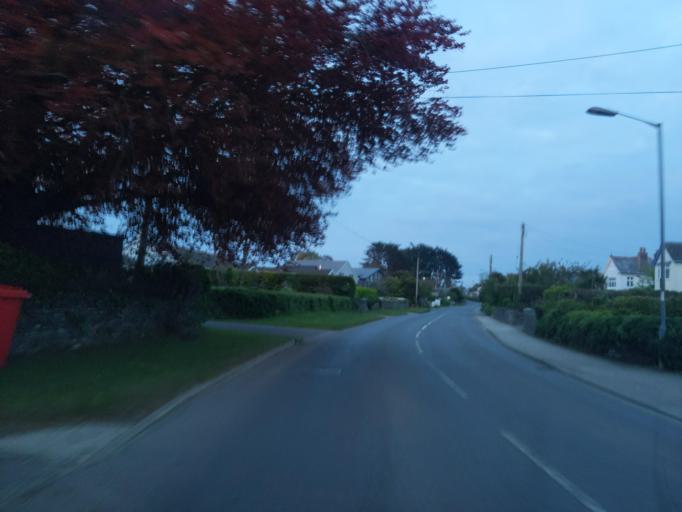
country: GB
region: England
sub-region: Cornwall
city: Polzeath
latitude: 50.5512
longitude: -4.9009
